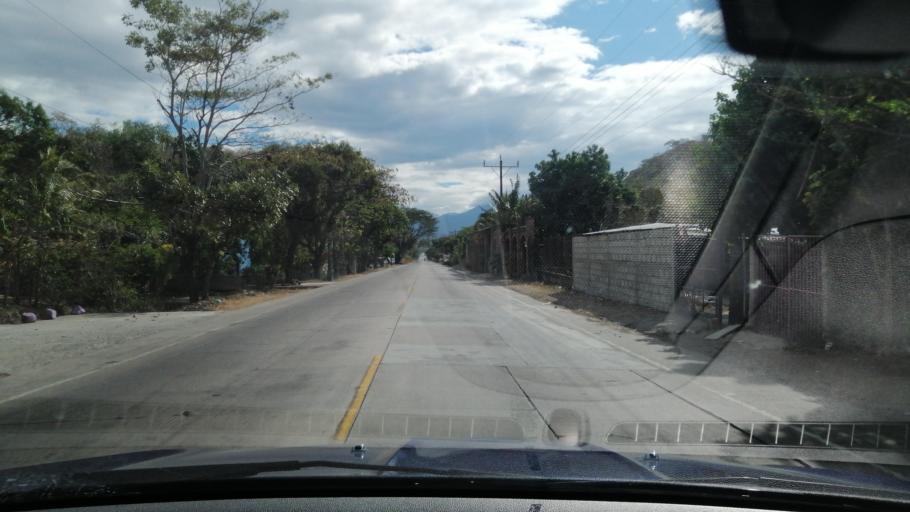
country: SV
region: Santa Ana
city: Santa Ana
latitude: 14.0489
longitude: -89.5181
